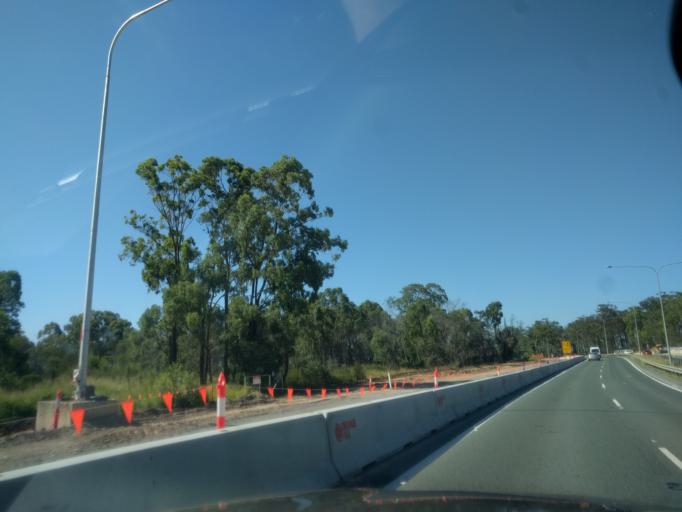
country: AU
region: Queensland
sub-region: Brisbane
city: Sunnybank Hills
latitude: -27.6424
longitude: 153.0432
